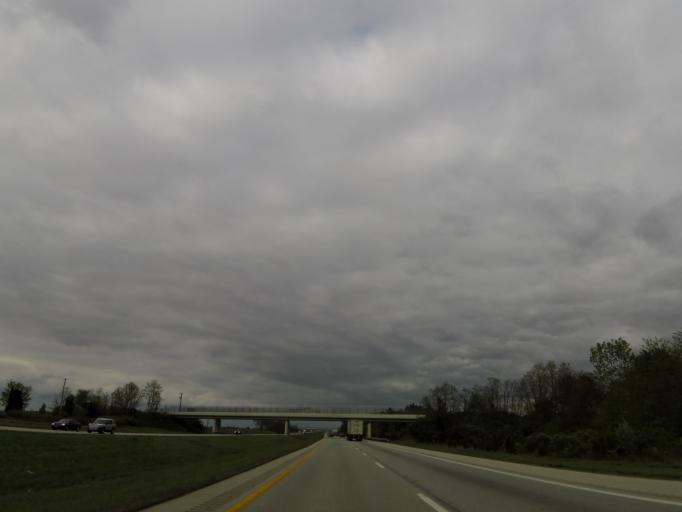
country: US
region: Ohio
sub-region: Clinton County
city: Wilmington
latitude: 39.5342
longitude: -83.7896
